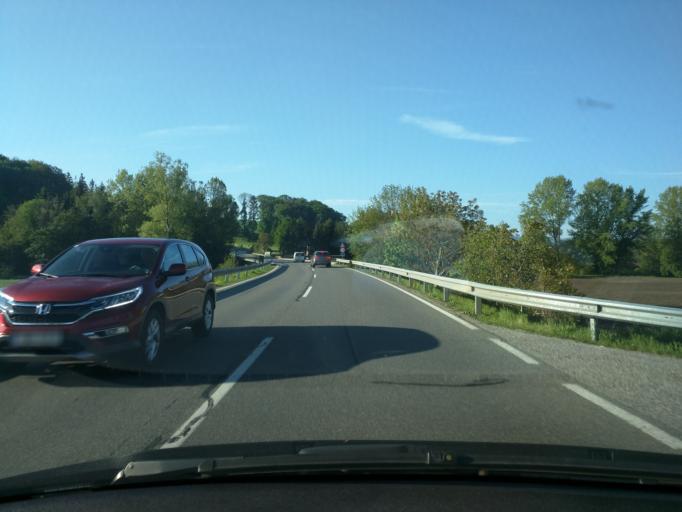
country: AT
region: Lower Austria
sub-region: Politischer Bezirk Melk
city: Blindenmarkt
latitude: 48.1175
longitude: 15.0123
